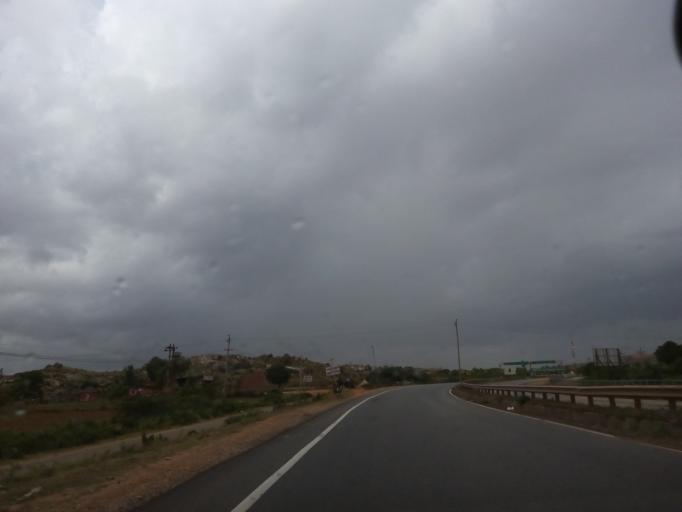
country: IN
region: Karnataka
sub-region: Chitradurga
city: Chitradurga
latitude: 14.2637
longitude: 76.3427
